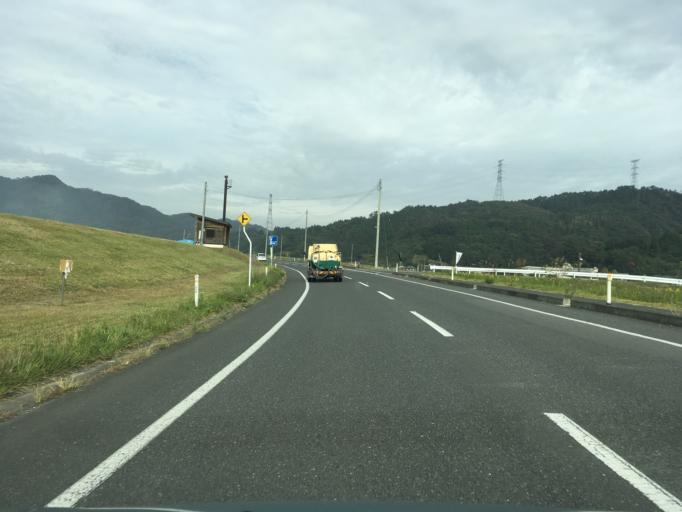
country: JP
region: Iwate
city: Ichinoseki
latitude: 38.9277
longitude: 141.2577
